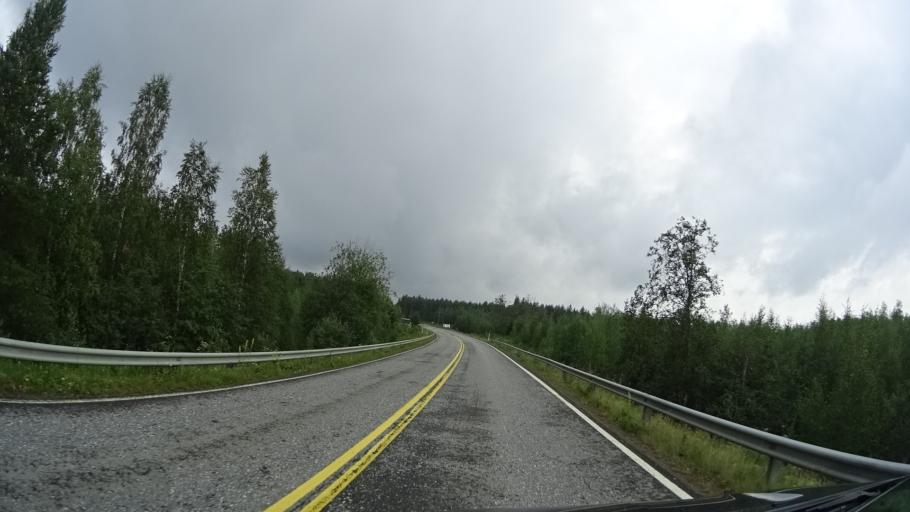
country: FI
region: North Karelia
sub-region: Keski-Karjala
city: Raeaekkylae
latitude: 62.3127
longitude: 29.5164
